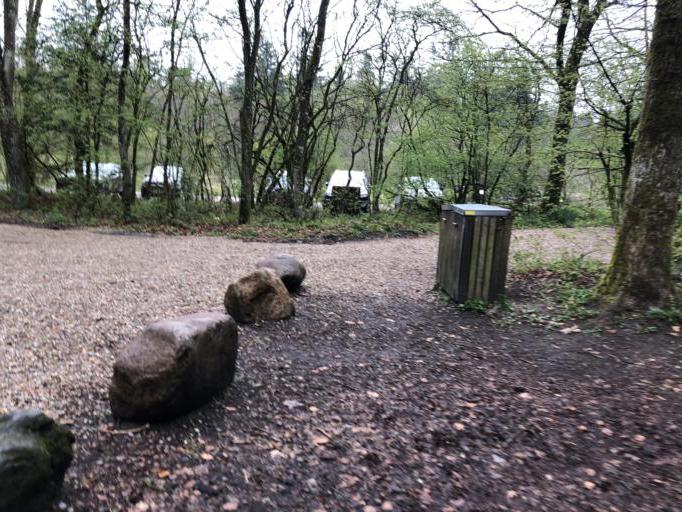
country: DK
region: Central Jutland
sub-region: Lemvig Kommune
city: Lemvig
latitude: 56.4845
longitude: 8.3630
